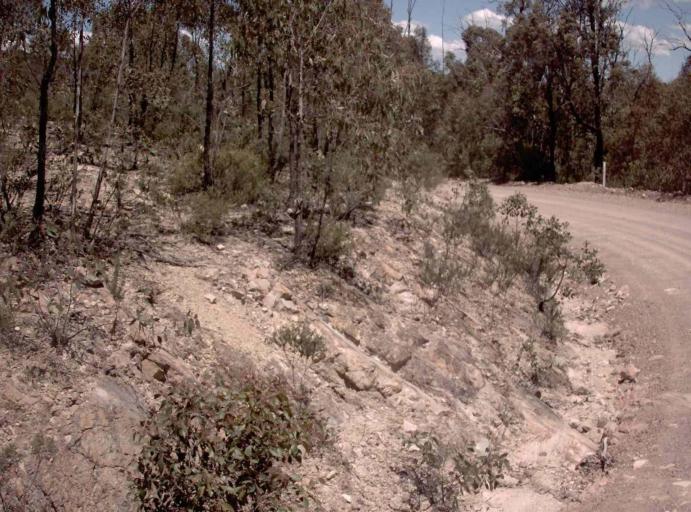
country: AU
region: New South Wales
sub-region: Snowy River
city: Jindabyne
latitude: -37.0736
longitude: 148.3253
